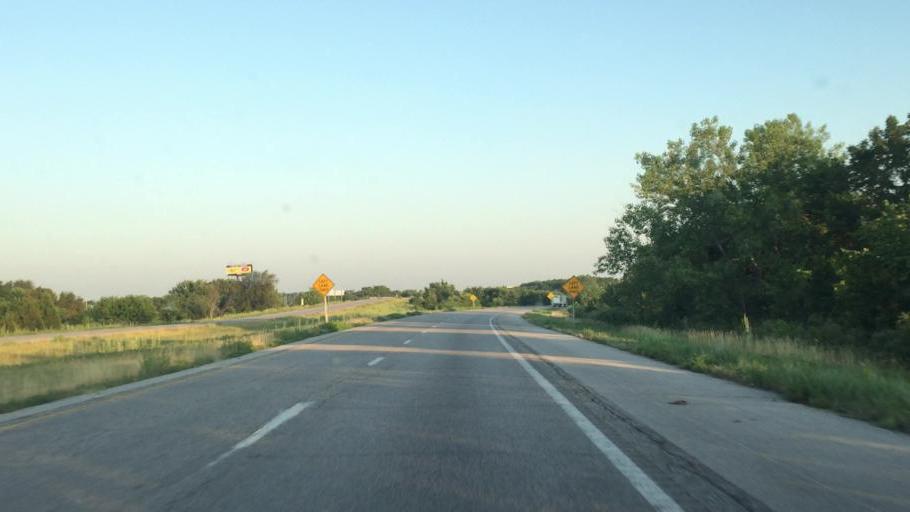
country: US
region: Missouri
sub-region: Platte County
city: Weatherby Lake
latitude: 39.3180
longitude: -94.6892
